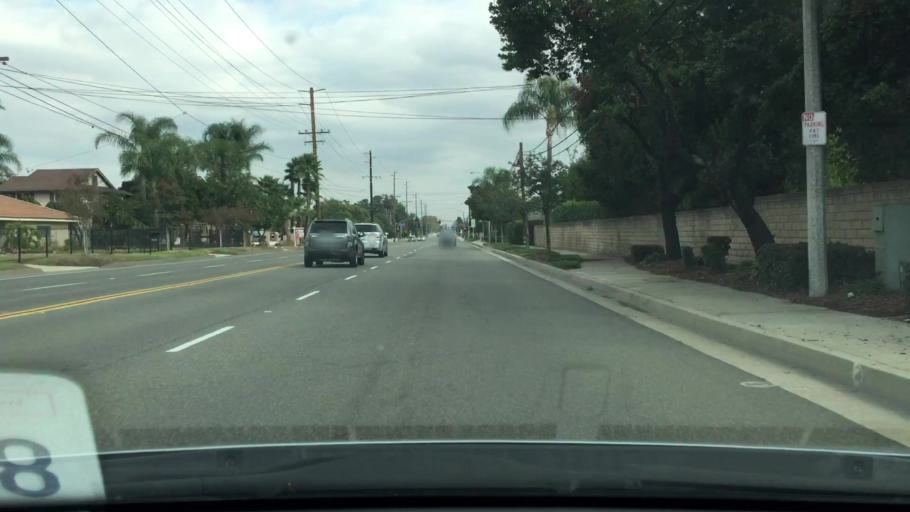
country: US
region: California
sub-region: San Bernardino County
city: Chino
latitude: 34.0115
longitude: -117.7230
